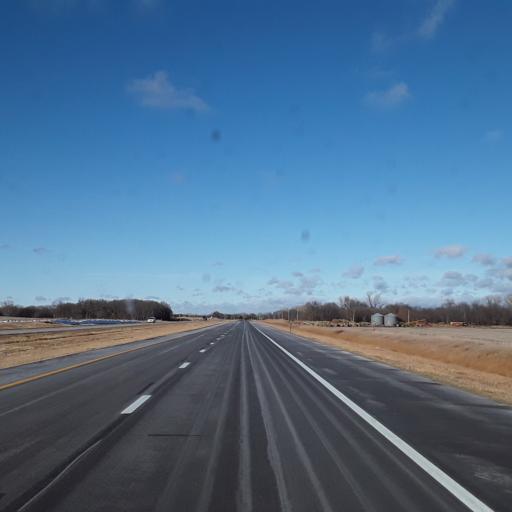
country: US
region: Kansas
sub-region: Republic County
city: Belleville
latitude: 39.7169
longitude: -97.6604
